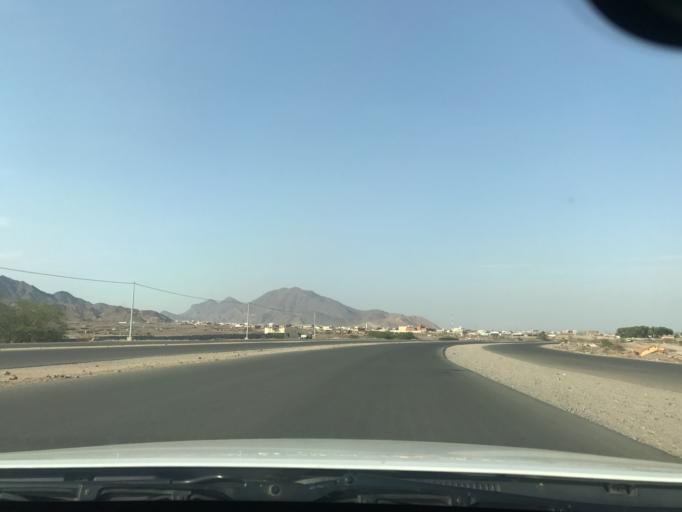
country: SA
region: Makkah
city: Al Jumum
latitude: 21.4499
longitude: 39.5218
